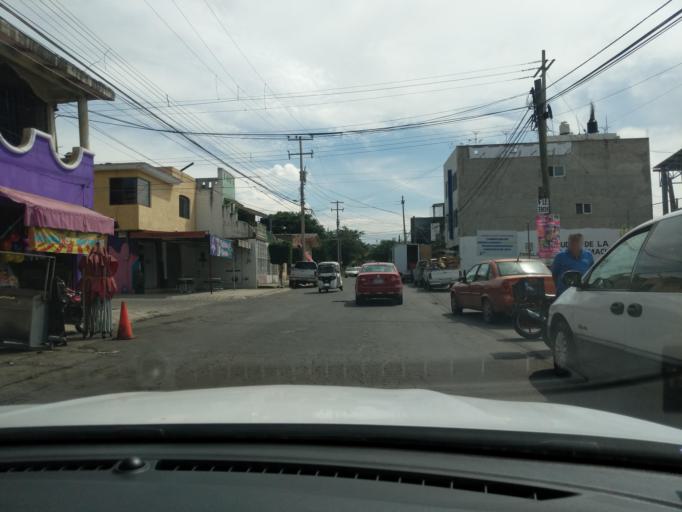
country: MX
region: Jalisco
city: Tonala
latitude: 20.6503
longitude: -103.2273
